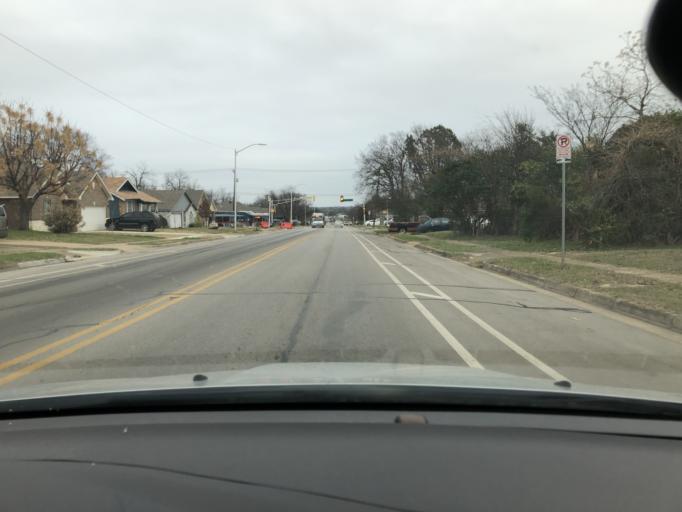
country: US
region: Texas
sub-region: Tarrant County
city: Fort Worth
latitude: 32.7271
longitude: -97.3085
